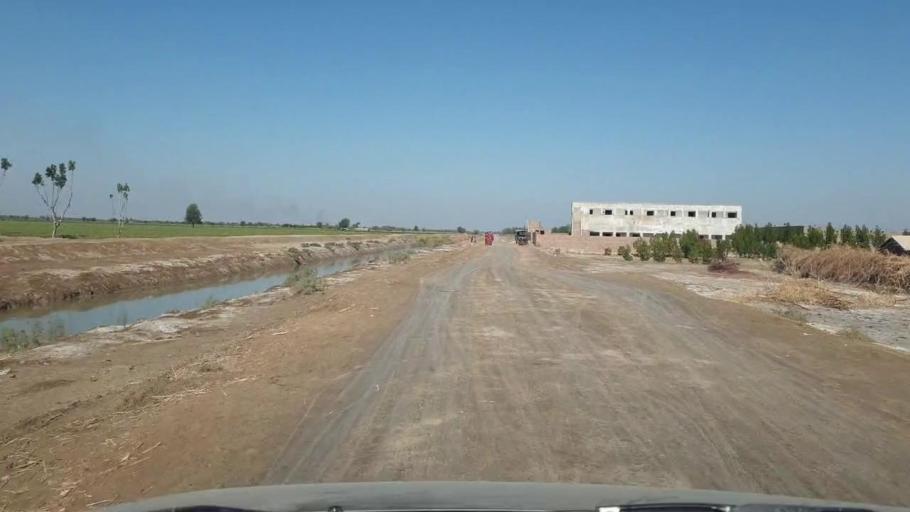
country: PK
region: Sindh
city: Mirwah Gorchani
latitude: 25.3181
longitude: 69.1244
